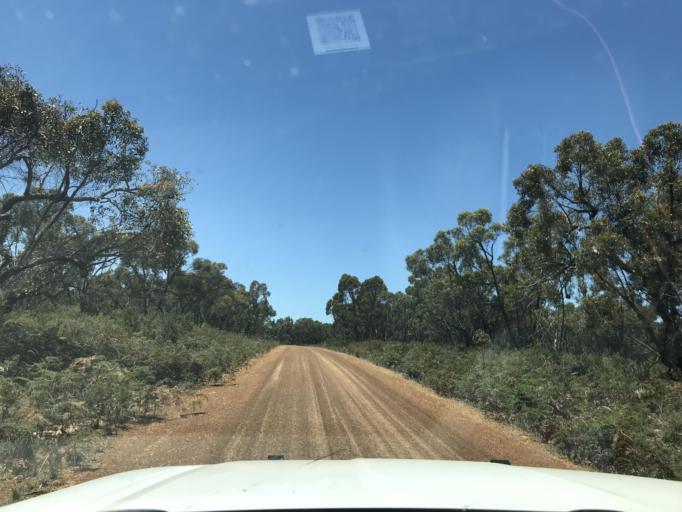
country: AU
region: South Australia
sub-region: Wattle Range
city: Penola
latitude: -37.0467
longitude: 141.3952
